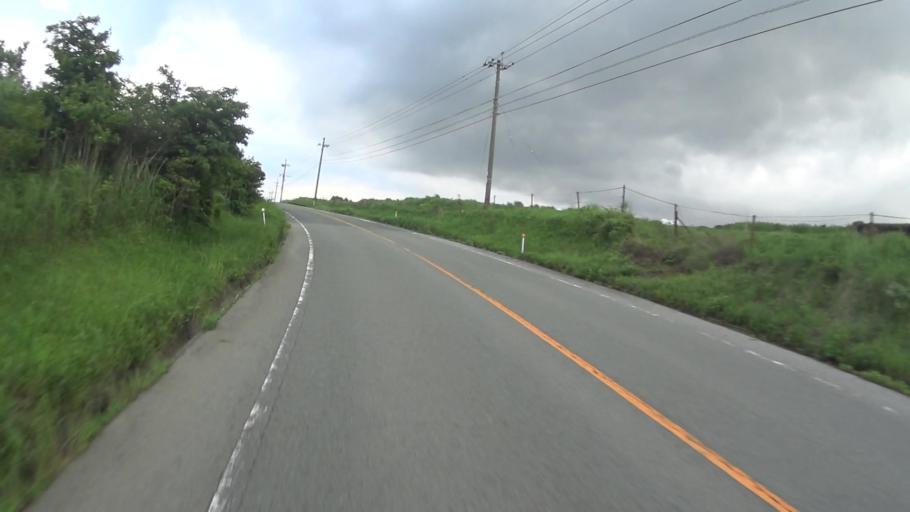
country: JP
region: Kumamoto
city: Aso
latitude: 32.9784
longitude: 131.0125
